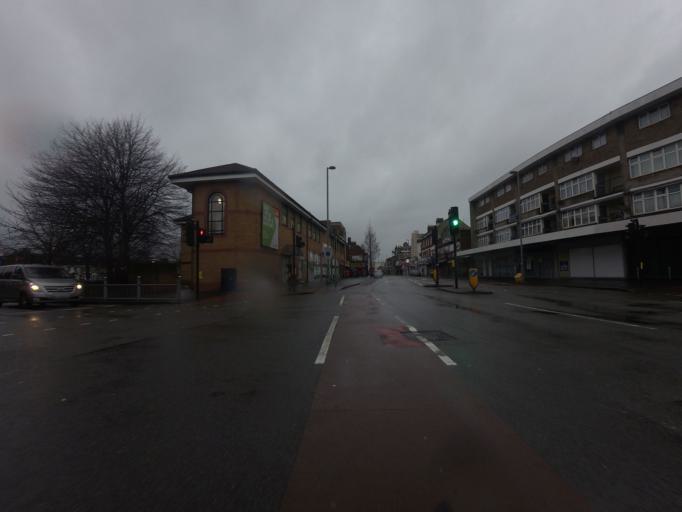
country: GB
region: England
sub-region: Greater London
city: Walthamstow
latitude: 51.5739
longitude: -0.0100
